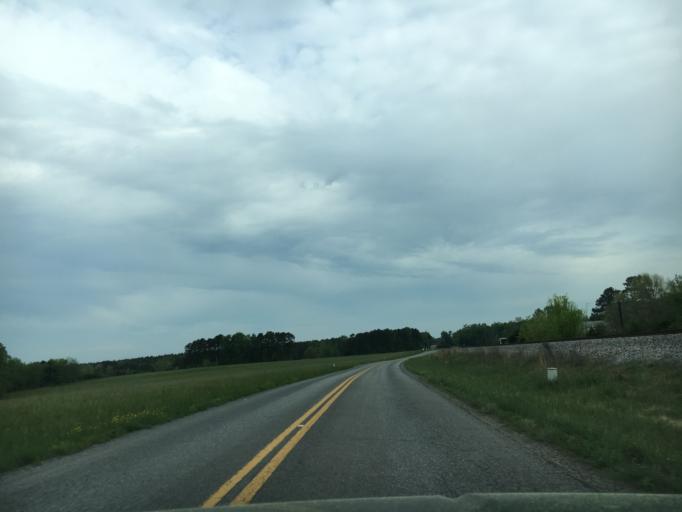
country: US
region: Virginia
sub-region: Campbell County
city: Brookneal
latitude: 36.9105
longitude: -78.9378
